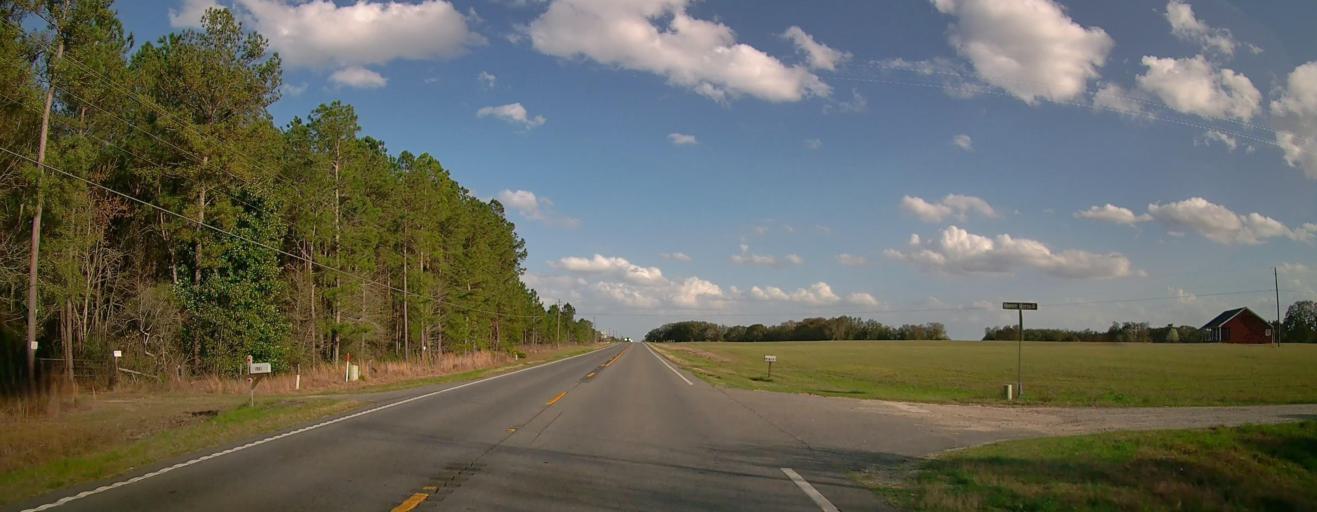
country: US
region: Georgia
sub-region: Tattnall County
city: Reidsville
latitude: 32.1058
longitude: -82.1710
